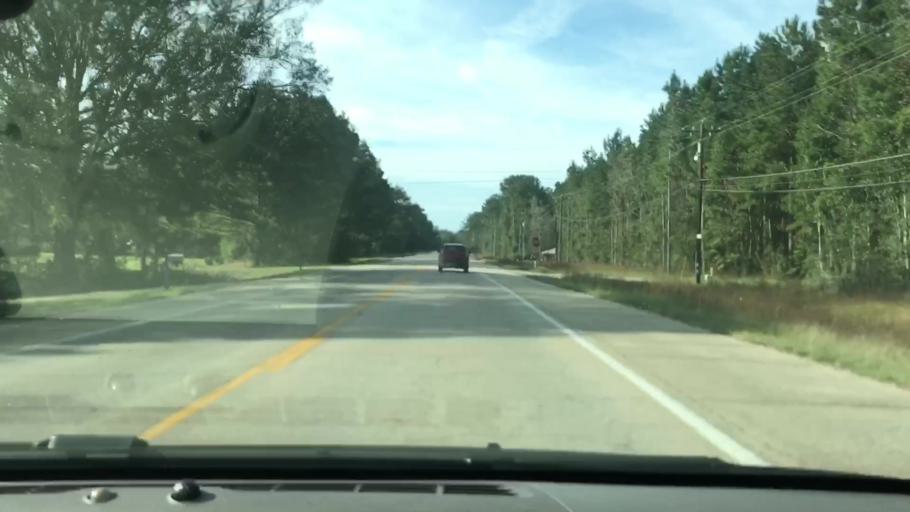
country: US
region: Louisiana
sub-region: Saint Tammany Parish
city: Pearl River
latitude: 30.4419
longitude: -89.7918
